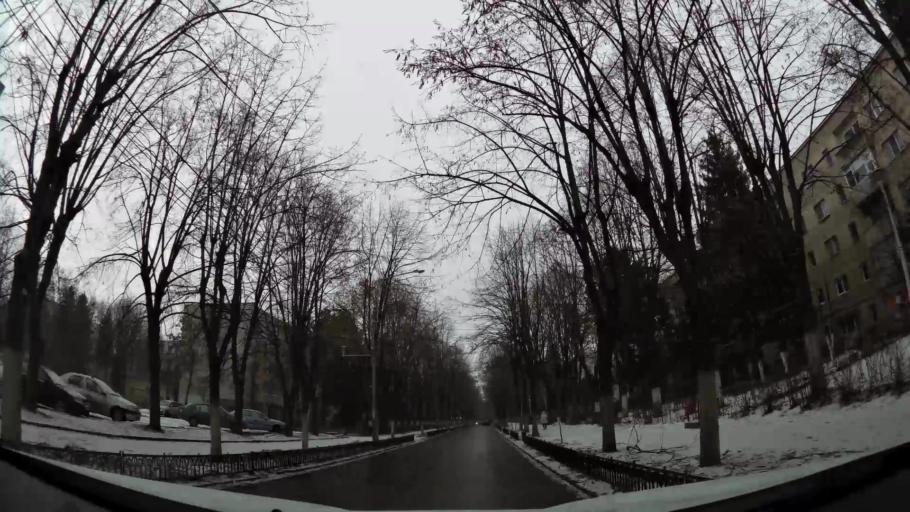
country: RO
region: Prahova
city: Ploiesti
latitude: 44.9577
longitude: 25.9986
